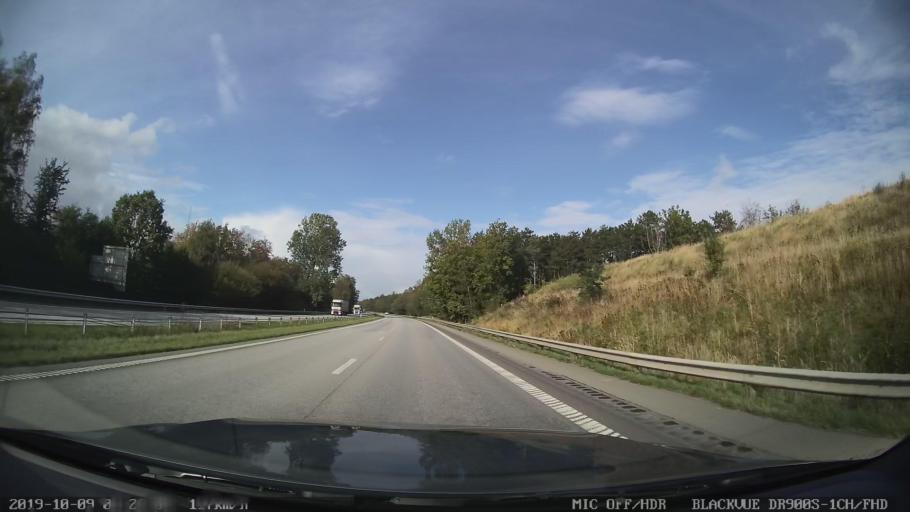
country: SE
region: Skane
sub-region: Landskrona
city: Asmundtorp
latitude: 55.8342
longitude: 12.9269
